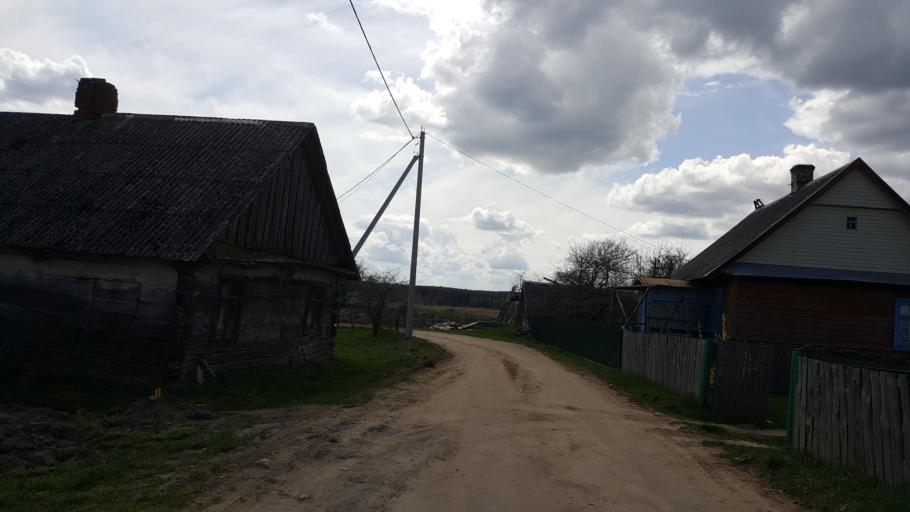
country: BY
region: Brest
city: Kamyanyets
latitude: 52.3501
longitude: 23.7306
